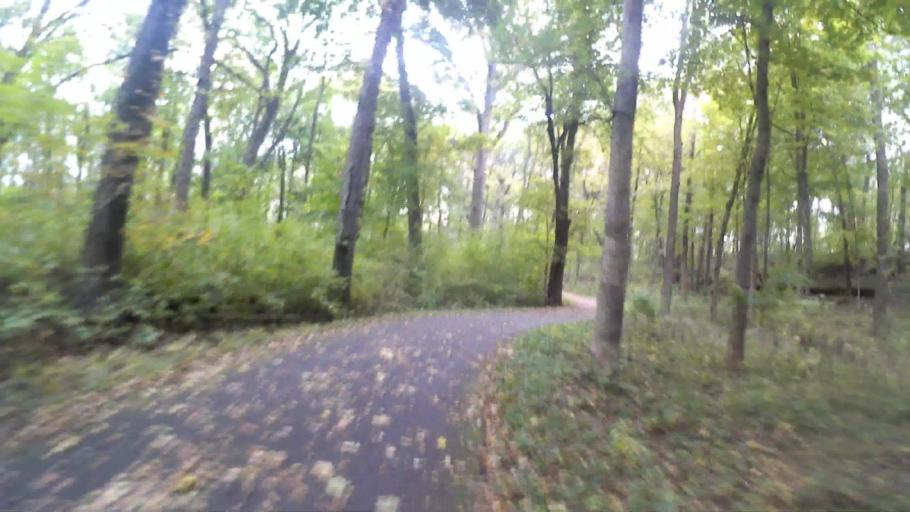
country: US
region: Illinois
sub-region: Kane County
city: Sugar Grove
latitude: 41.7824
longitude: -88.4324
